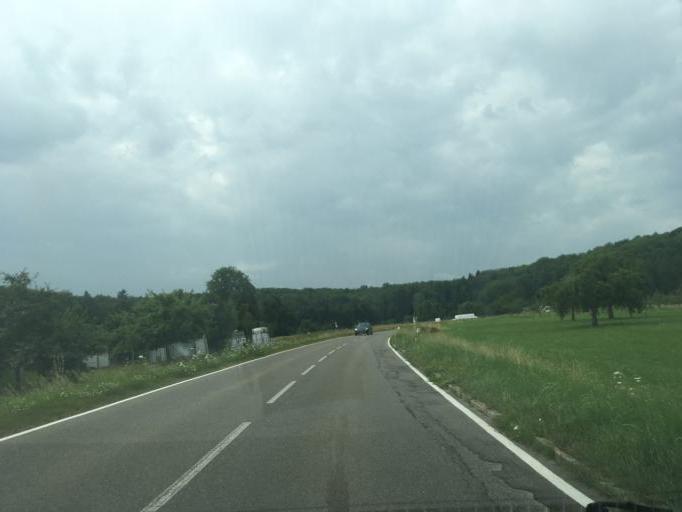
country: DE
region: Baden-Wuerttemberg
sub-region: Regierungsbezirk Stuttgart
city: Waldenbuch
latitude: 48.6272
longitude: 9.1319
